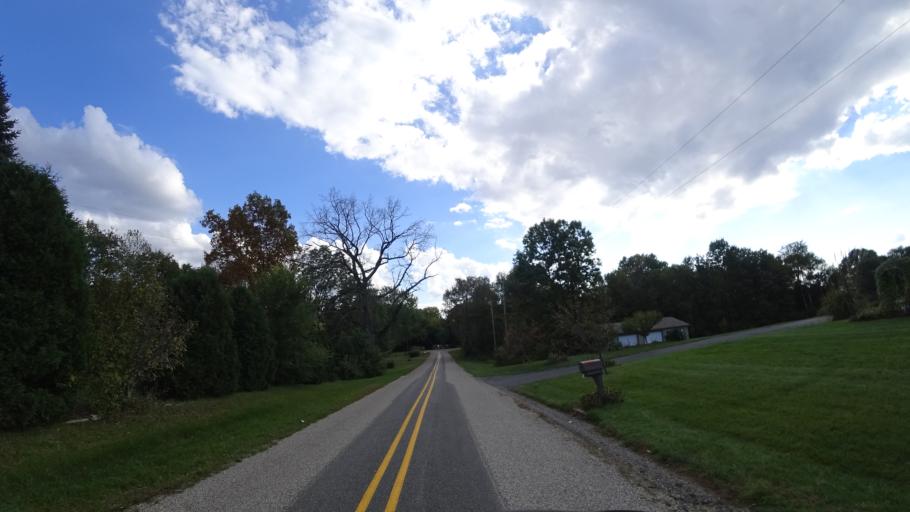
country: US
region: Michigan
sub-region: Saint Joseph County
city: Three Rivers
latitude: 41.9490
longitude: -85.5910
